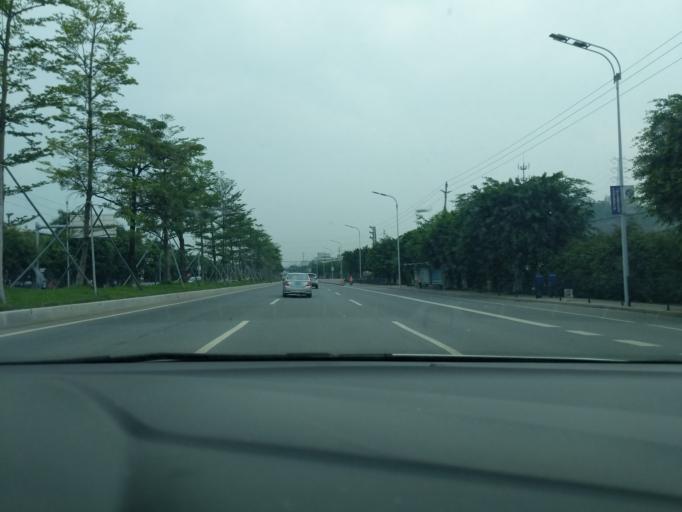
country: CN
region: Guangdong
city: Dongyong
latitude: 22.8629
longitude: 113.4830
